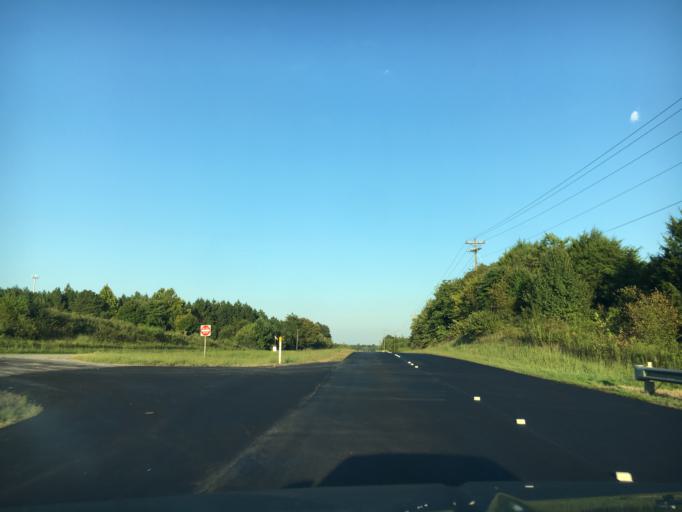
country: US
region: Virginia
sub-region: City of Danville
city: Danville
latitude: 36.5806
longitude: -79.2393
